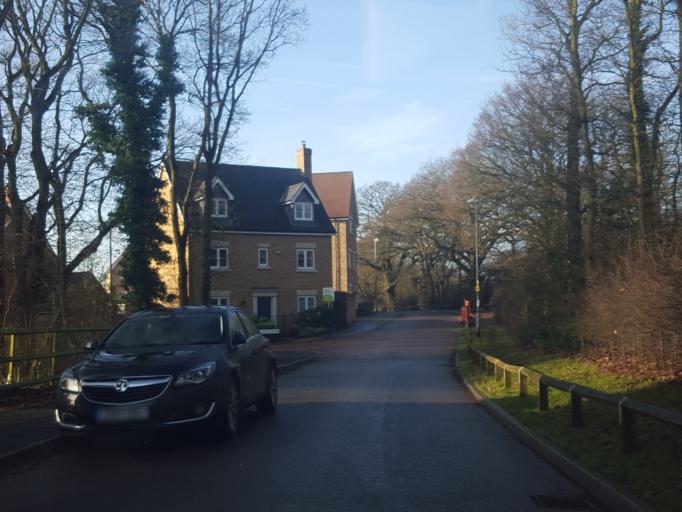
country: GB
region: England
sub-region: Essex
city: West Bergholt
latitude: 51.9037
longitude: 0.8778
